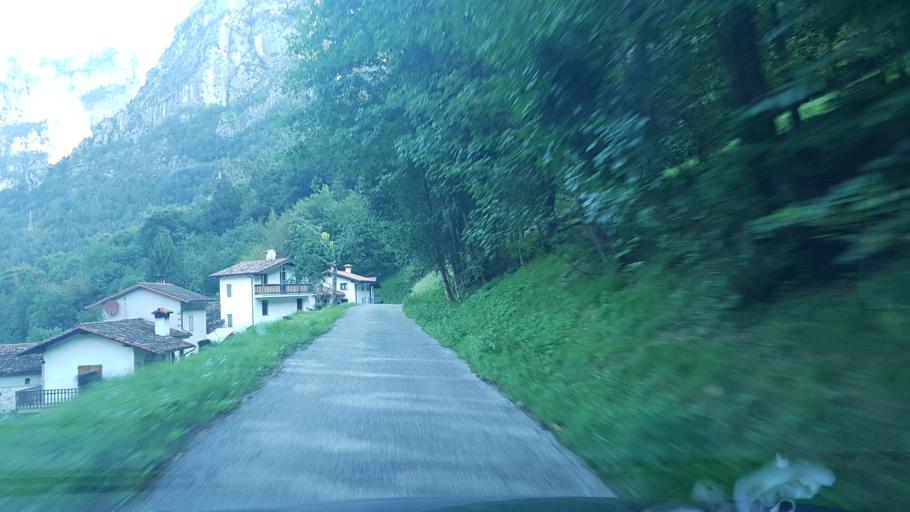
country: IT
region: Friuli Venezia Giulia
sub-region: Provincia di Pordenone
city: Frisanco
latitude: 46.2559
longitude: 12.7036
